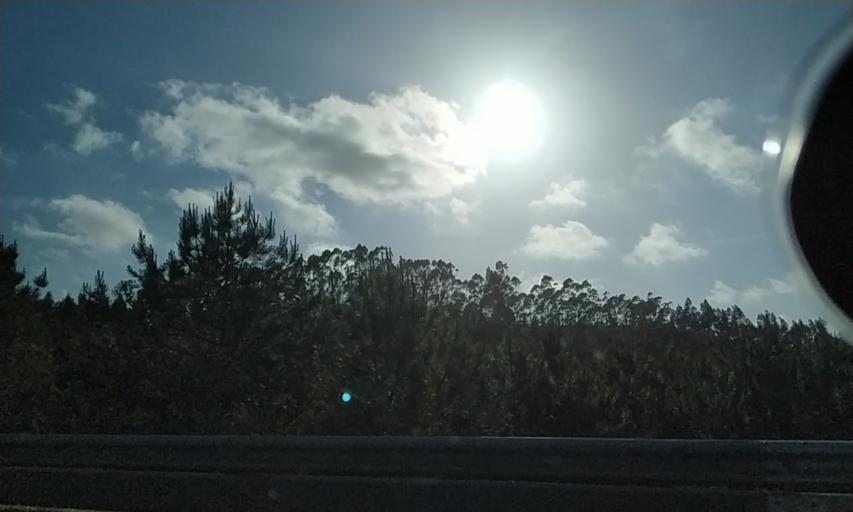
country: PT
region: Lisbon
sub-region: Torres Vedras
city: Torres Vedras
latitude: 39.1402
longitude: -9.2480
